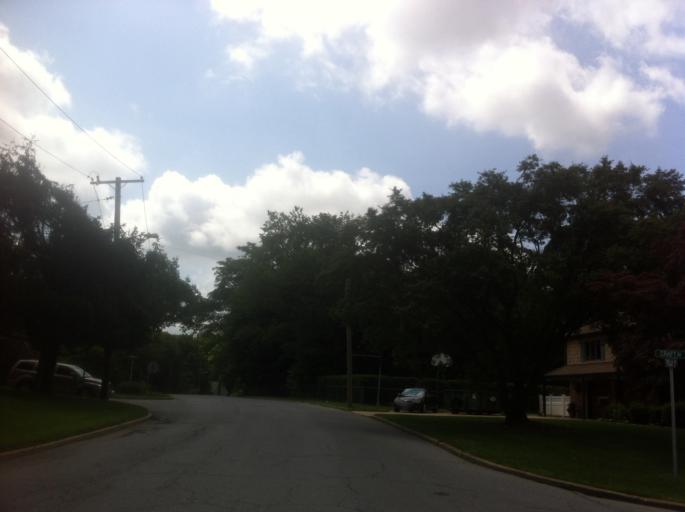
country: US
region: New York
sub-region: Nassau County
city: Glen Cove
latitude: 40.8559
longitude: -73.6307
